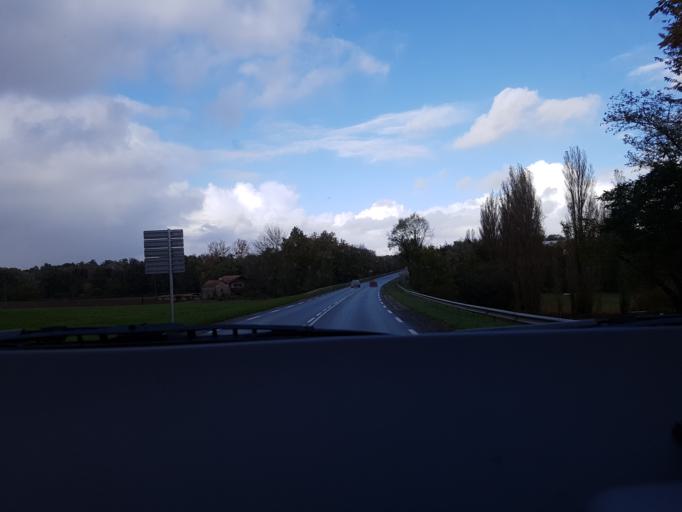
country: FR
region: Poitou-Charentes
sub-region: Departement de la Charente-Maritime
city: Pons
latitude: 45.5777
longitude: -0.5579
